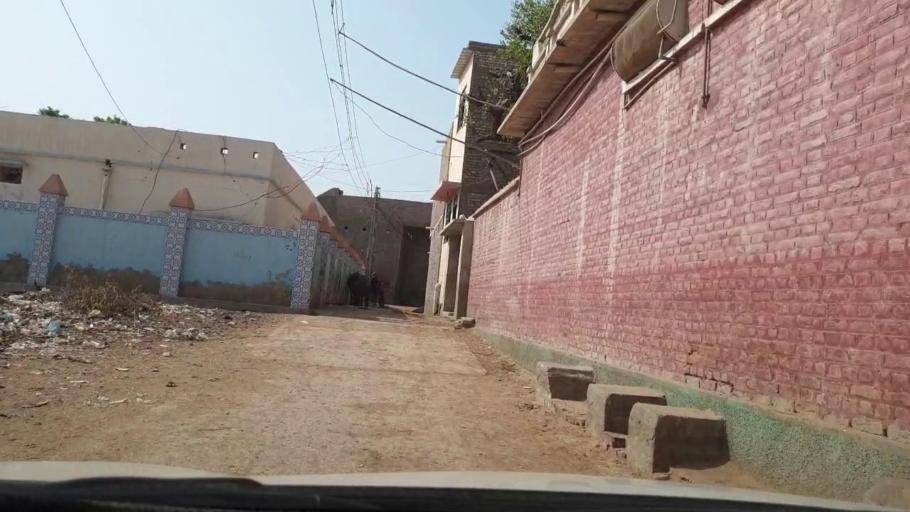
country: PK
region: Sindh
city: Larkana
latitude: 27.4591
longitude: 68.2304
